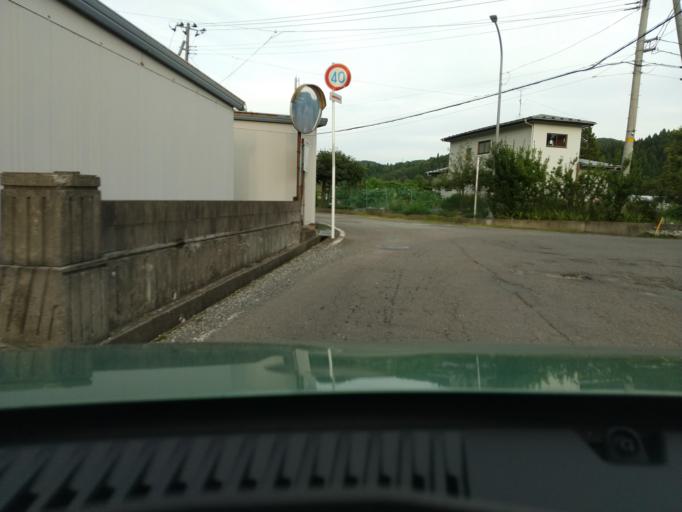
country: JP
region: Akita
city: Akita
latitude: 39.7808
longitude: 140.1348
